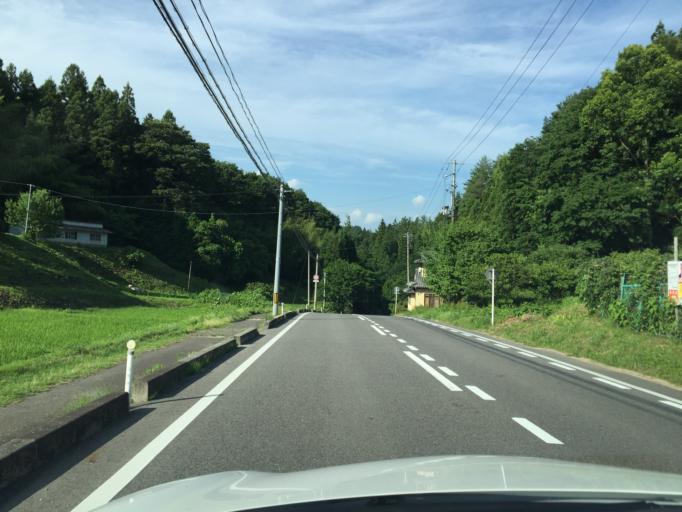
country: JP
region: Fukushima
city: Miharu
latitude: 37.3234
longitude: 140.4885
